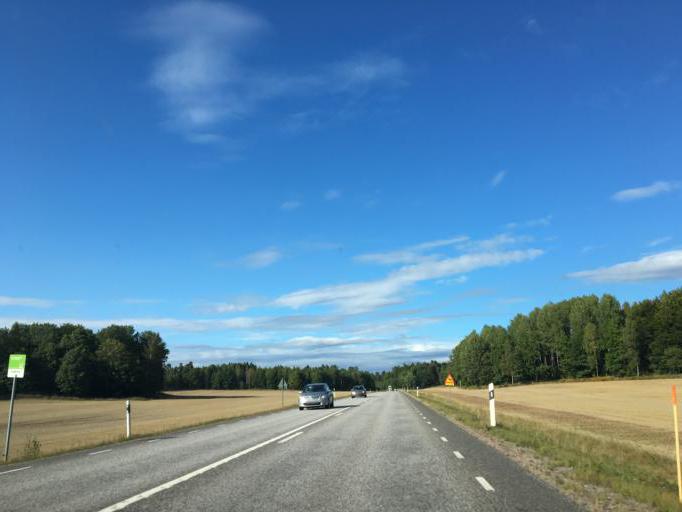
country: SE
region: Soedermanland
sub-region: Nykopings Kommun
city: Nykoping
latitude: 58.8041
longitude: 16.9477
